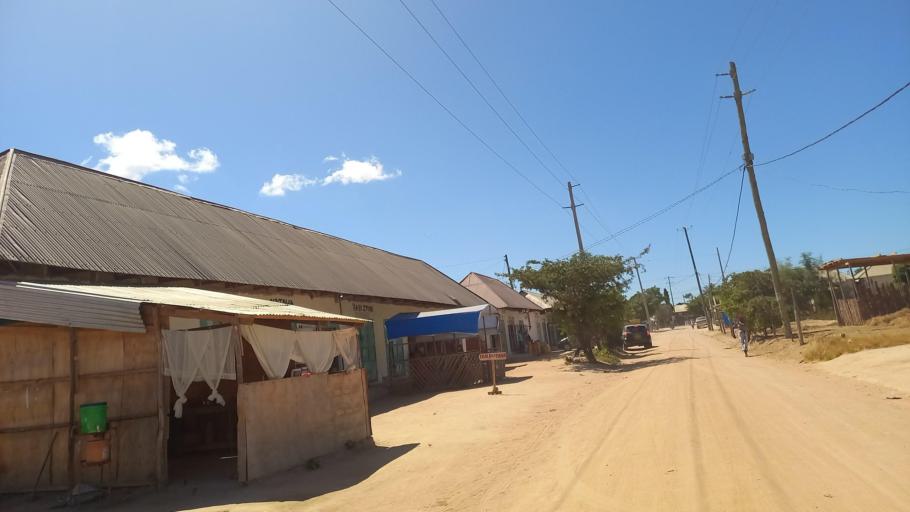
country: TZ
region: Dodoma
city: Dodoma
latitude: -6.1109
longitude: 35.7466
